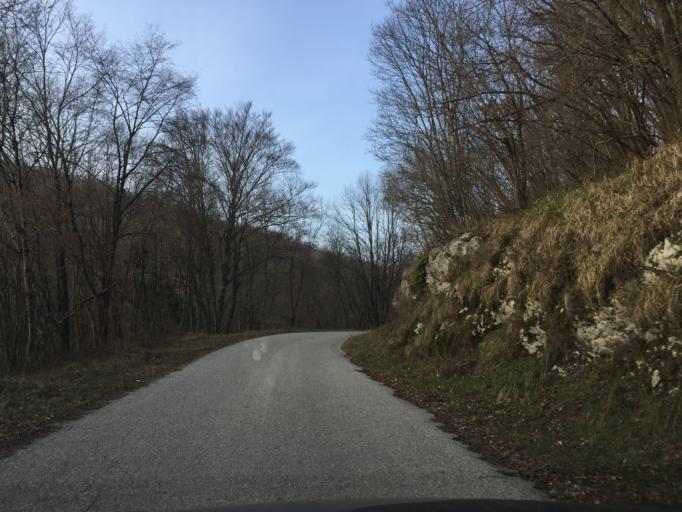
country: SI
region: Kanal
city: Kanal
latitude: 46.0578
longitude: 13.6672
